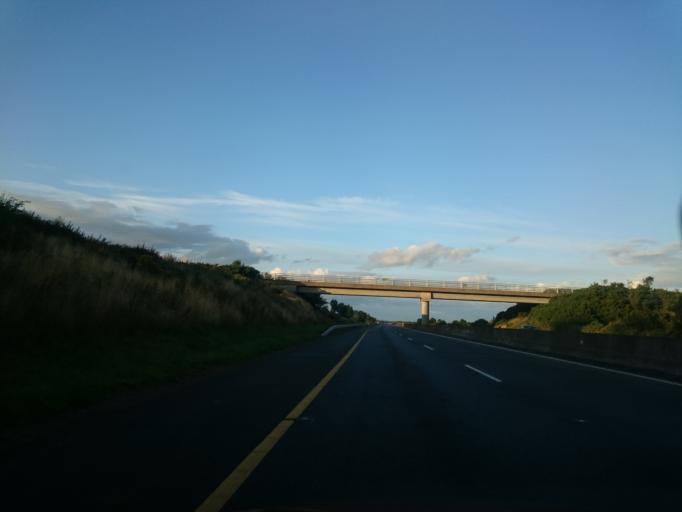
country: IE
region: Leinster
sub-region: Loch Garman
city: Gorey
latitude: 52.6492
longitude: -6.3202
